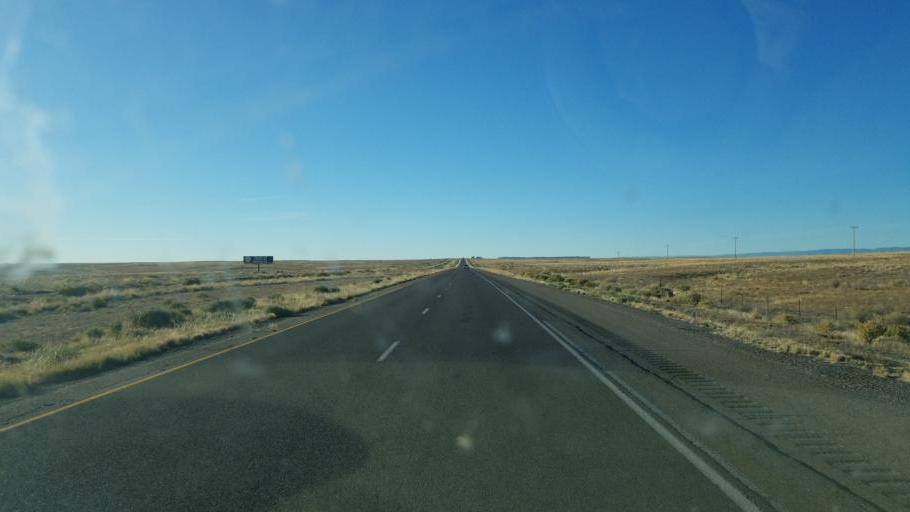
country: US
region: New Mexico
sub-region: San Juan County
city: Shiprock
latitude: 36.7149
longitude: -108.7095
